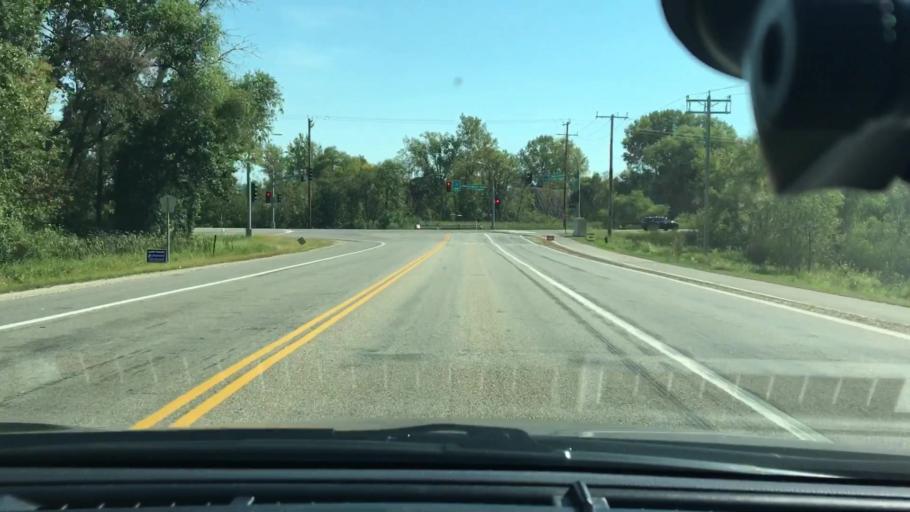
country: US
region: Minnesota
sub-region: Wright County
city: Hanover
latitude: 45.1620
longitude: -93.6671
